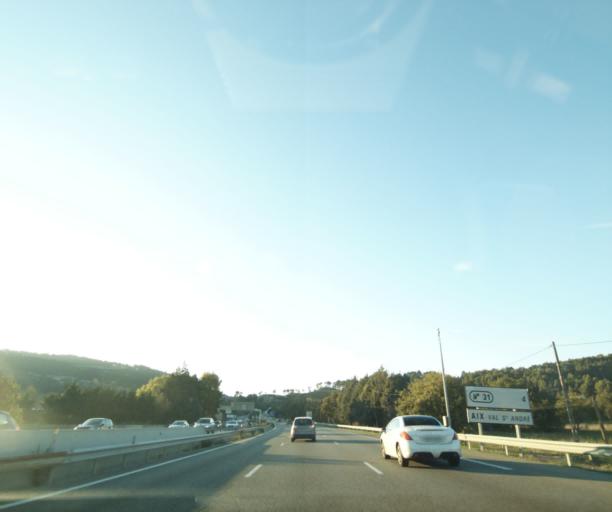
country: FR
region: Provence-Alpes-Cote d'Azur
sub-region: Departement des Bouches-du-Rhone
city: Le Tholonet
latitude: 43.5033
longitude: 5.5172
